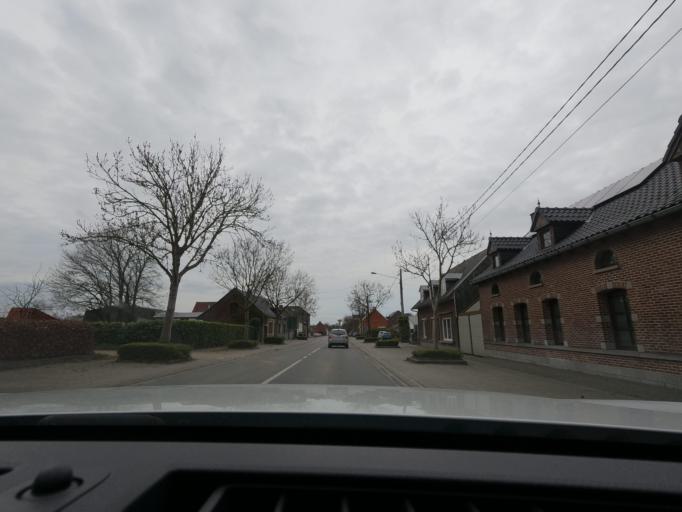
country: BE
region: Wallonia
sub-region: Province du Hainaut
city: Silly
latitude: 50.6543
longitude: 3.8735
